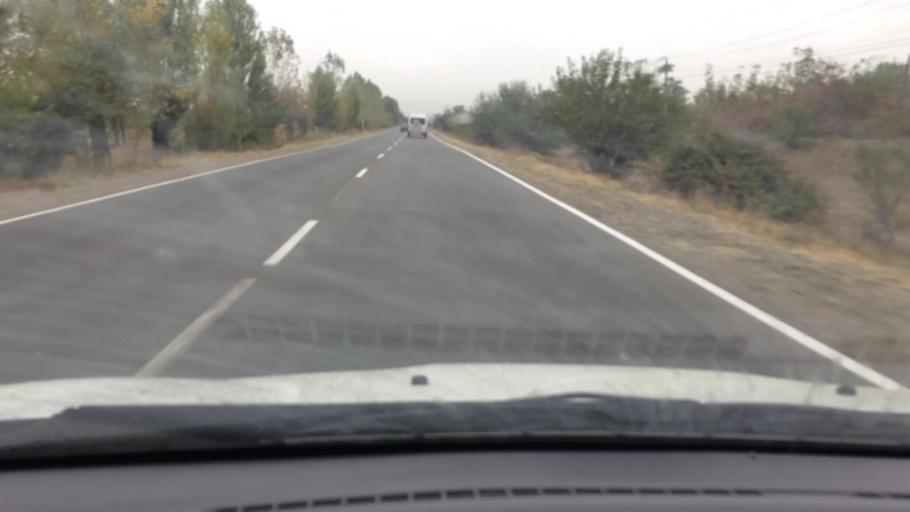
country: GE
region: Kvemo Kartli
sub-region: Marneuli
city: Marneuli
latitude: 41.4477
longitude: 44.8148
